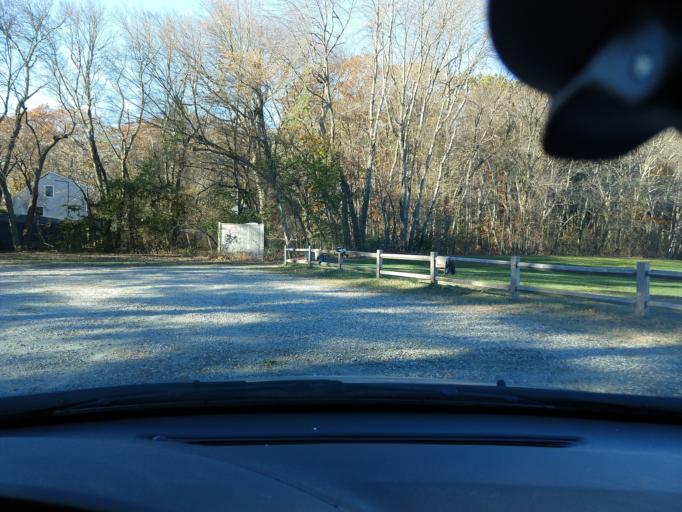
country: US
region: Massachusetts
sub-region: Middlesex County
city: Bedford
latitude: 42.4738
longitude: -71.2740
